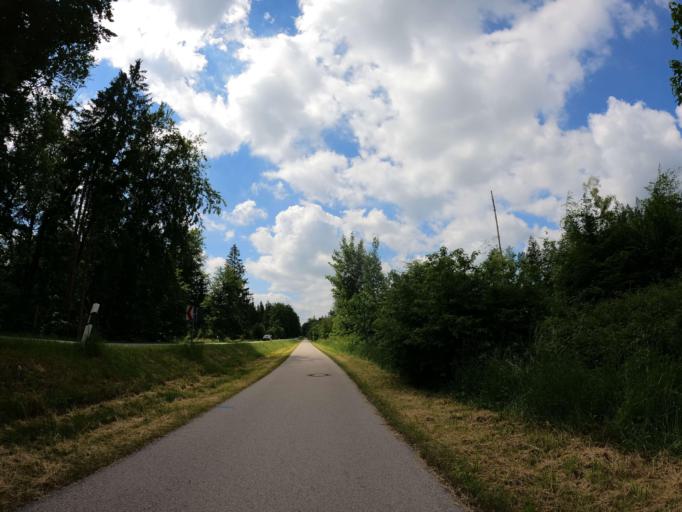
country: DE
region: Bavaria
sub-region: Upper Bavaria
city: Oberhaching
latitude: 48.0048
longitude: 11.5798
